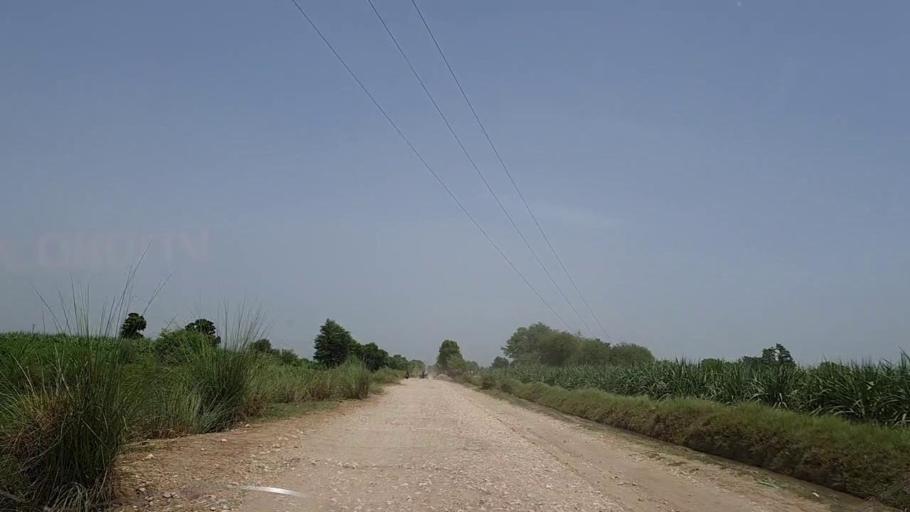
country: PK
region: Sindh
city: Tharu Shah
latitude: 26.8980
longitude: 68.0086
